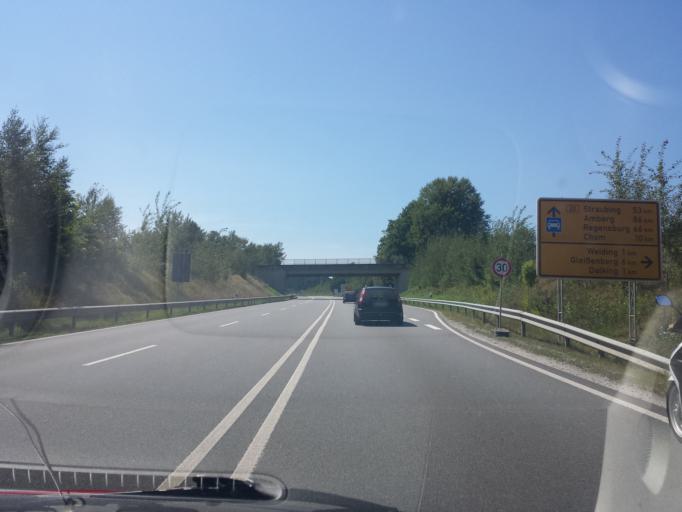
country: DE
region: Bavaria
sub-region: Upper Palatinate
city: Weiding
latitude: 49.2677
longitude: 12.7541
